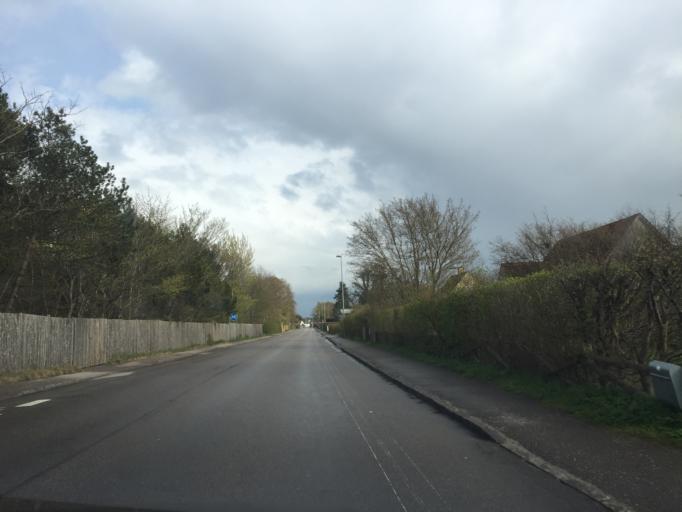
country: DK
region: Capital Region
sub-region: Halsnaes Kommune
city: Liseleje
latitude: 56.0103
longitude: 11.9792
